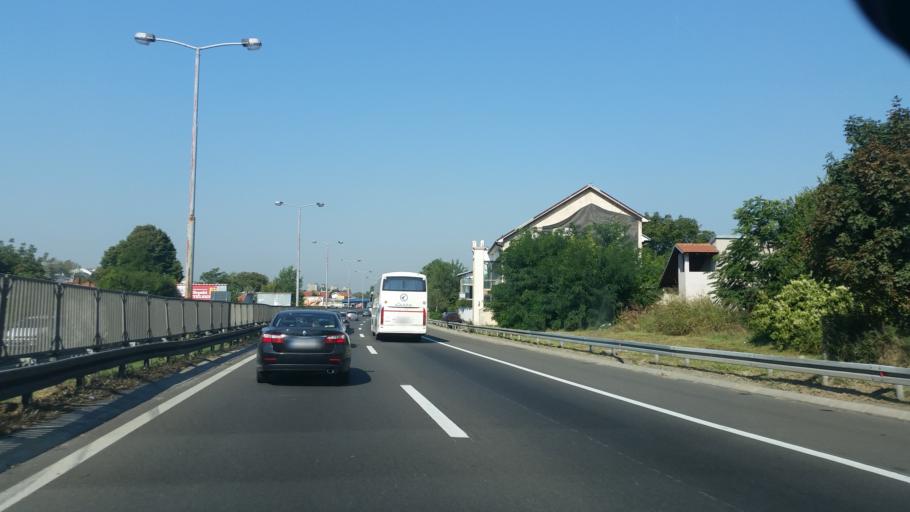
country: RS
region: Central Serbia
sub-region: Belgrade
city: Vozdovac
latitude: 44.7825
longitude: 20.4862
